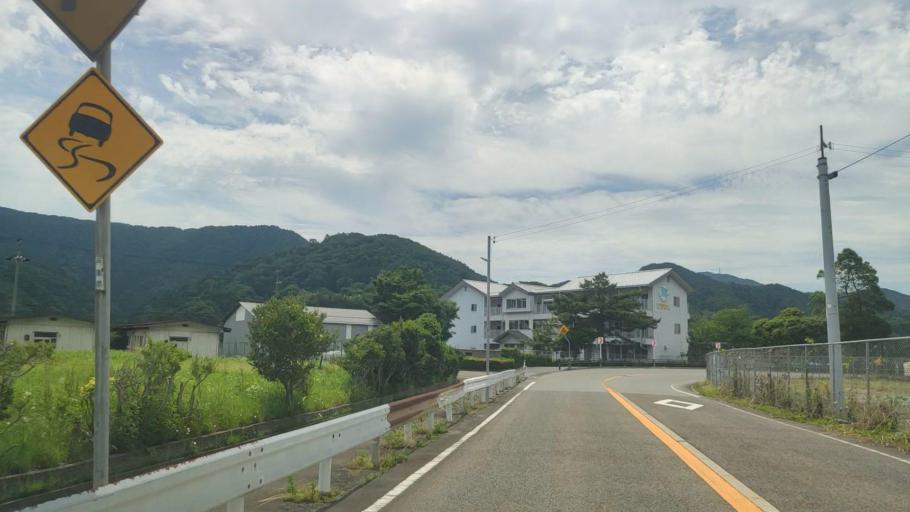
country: JP
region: Hyogo
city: Toyooka
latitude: 35.6474
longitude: 134.7583
